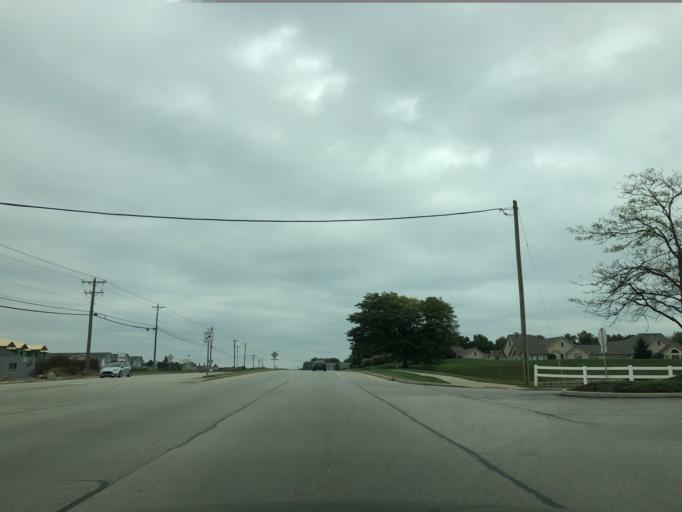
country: US
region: Ohio
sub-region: Warren County
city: Landen
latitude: 39.2973
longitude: -84.2902
